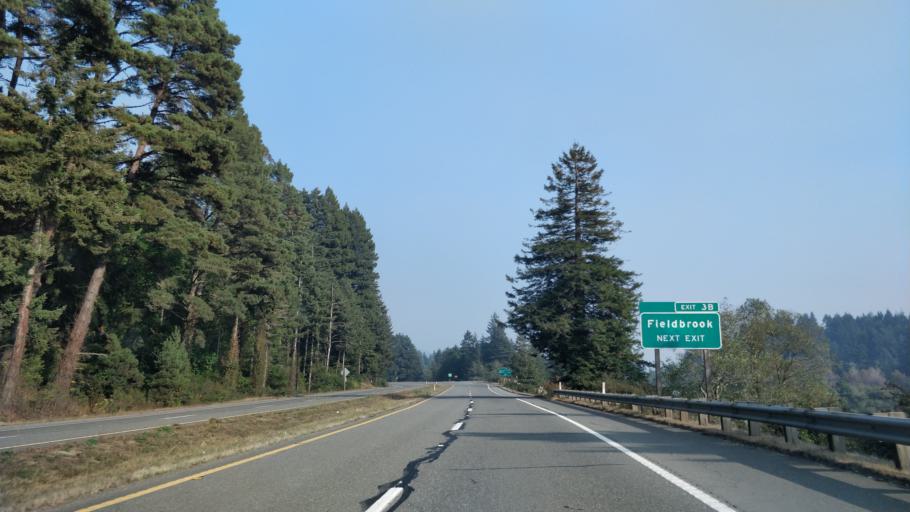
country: US
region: California
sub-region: Humboldt County
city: Arcata
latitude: 40.9077
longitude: -124.0447
